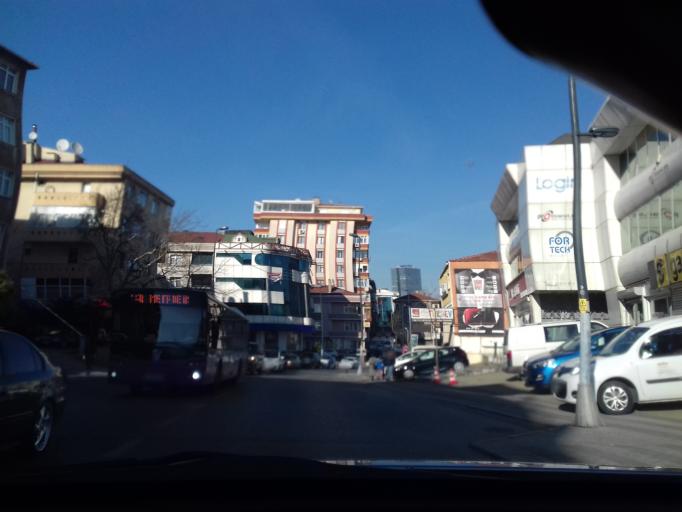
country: TR
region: Istanbul
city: Umraniye
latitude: 41.0246
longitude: 29.0810
